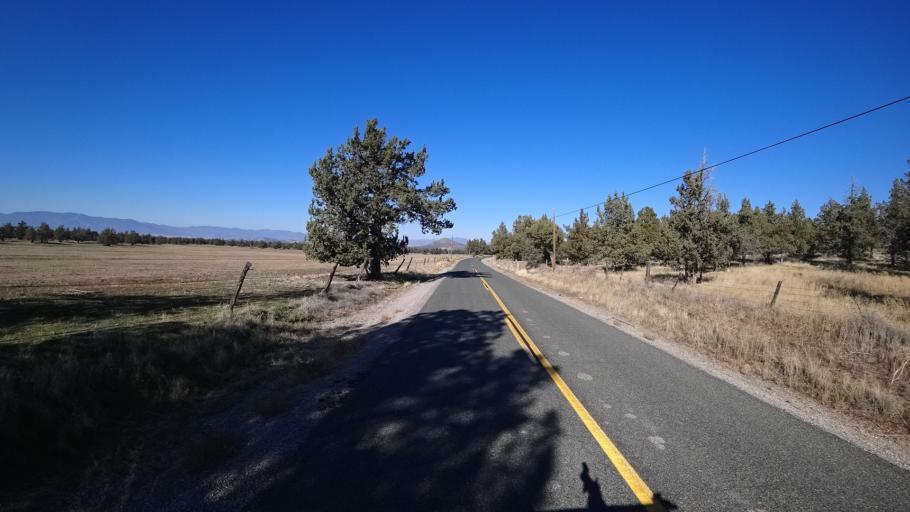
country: US
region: California
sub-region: Siskiyou County
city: Weed
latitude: 41.6278
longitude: -122.3315
